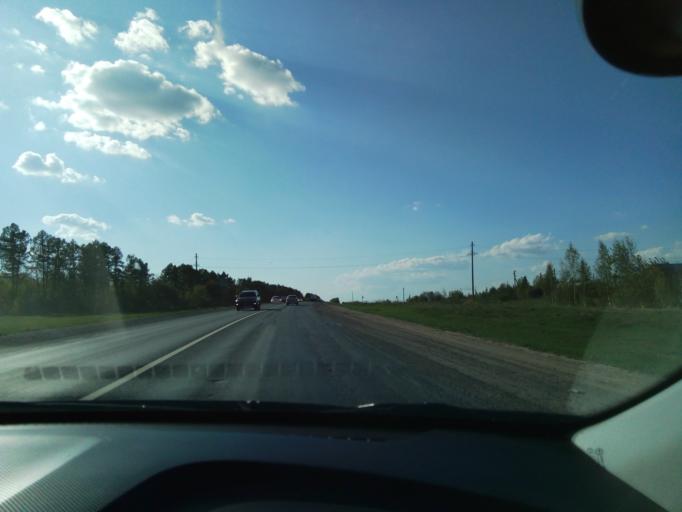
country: RU
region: Chuvashia
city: Novyye Lapsary
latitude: 56.0634
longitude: 47.2438
